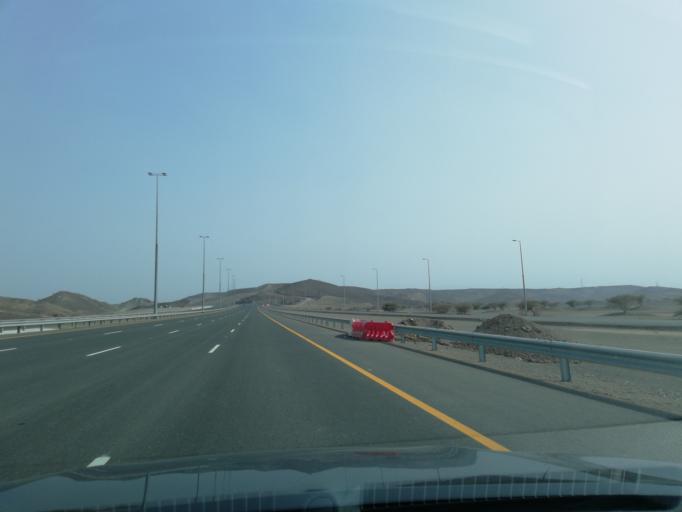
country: OM
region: Al Batinah
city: Al Liwa'
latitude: 24.3614
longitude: 56.5513
